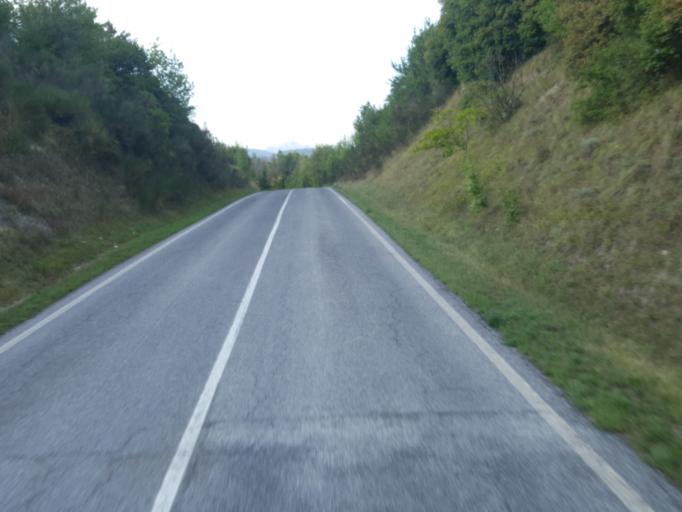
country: IT
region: The Marches
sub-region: Provincia di Ancona
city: Fabriano
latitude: 43.3256
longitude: 12.8331
